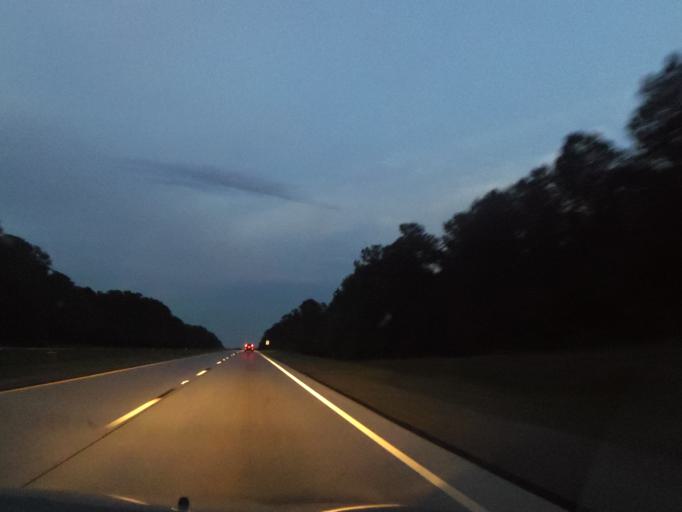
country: US
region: Georgia
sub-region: McDuffie County
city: Thomson
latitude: 33.5097
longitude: -82.4321
